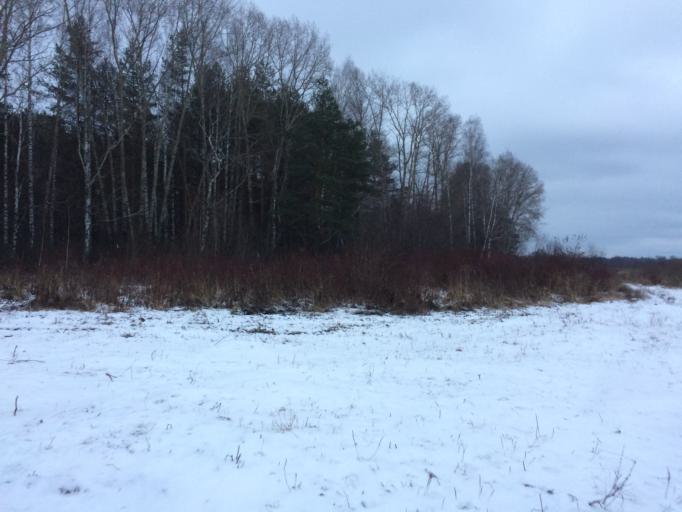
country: RU
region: Mariy-El
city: Yoshkar-Ola
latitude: 56.6217
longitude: 47.9167
